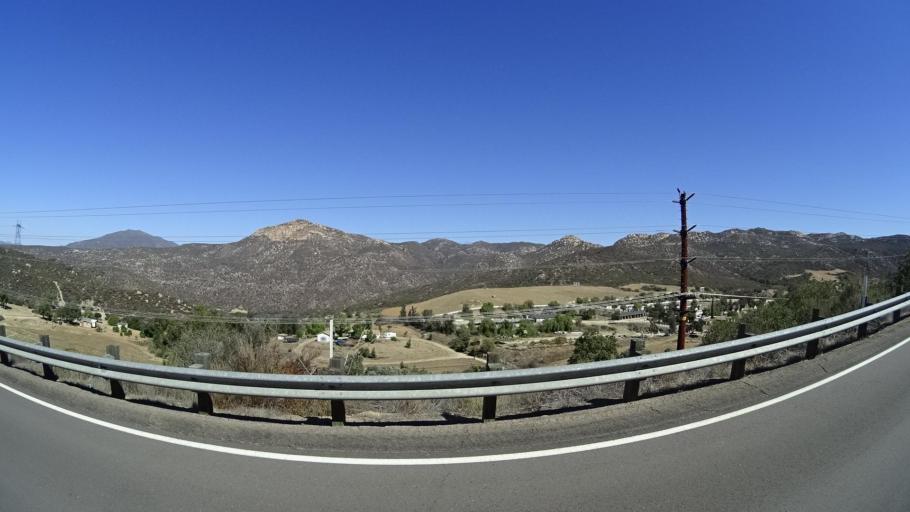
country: US
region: California
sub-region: San Diego County
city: Alpine
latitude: 32.7754
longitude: -116.7097
